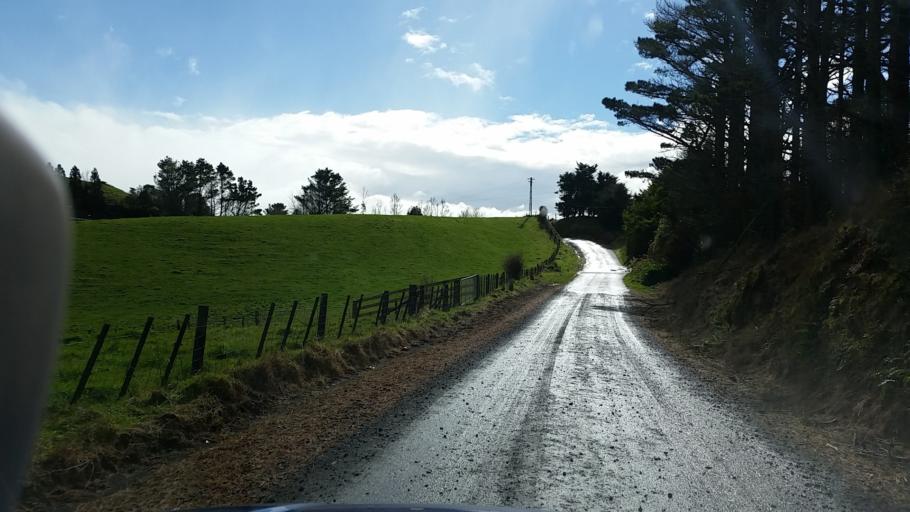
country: NZ
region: Taranaki
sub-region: South Taranaki District
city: Eltham
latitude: -39.2782
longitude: 174.3079
